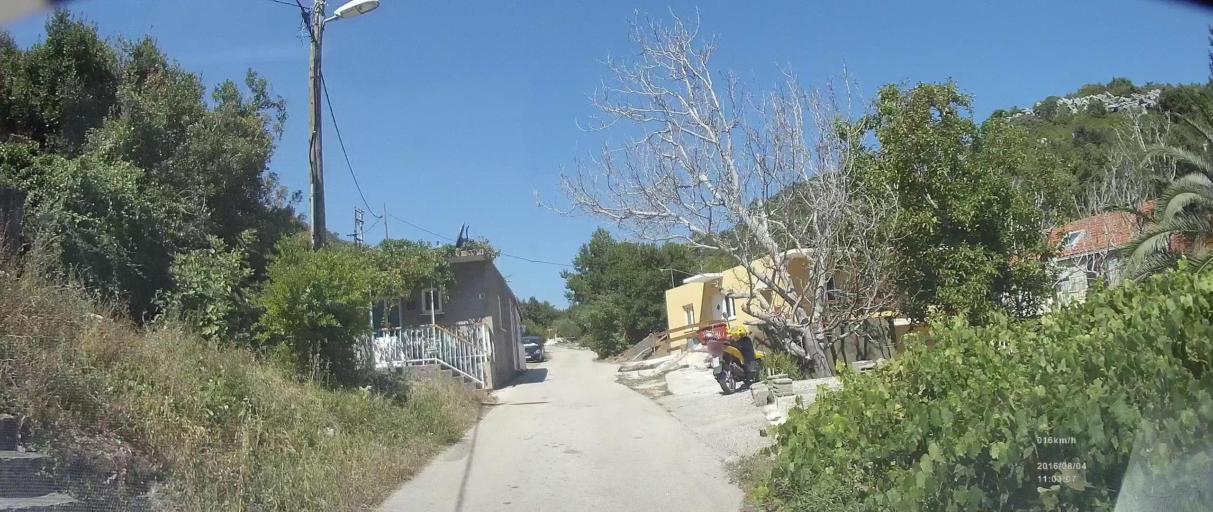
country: HR
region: Dubrovacko-Neretvanska
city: Blato
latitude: 42.7763
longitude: 17.4633
